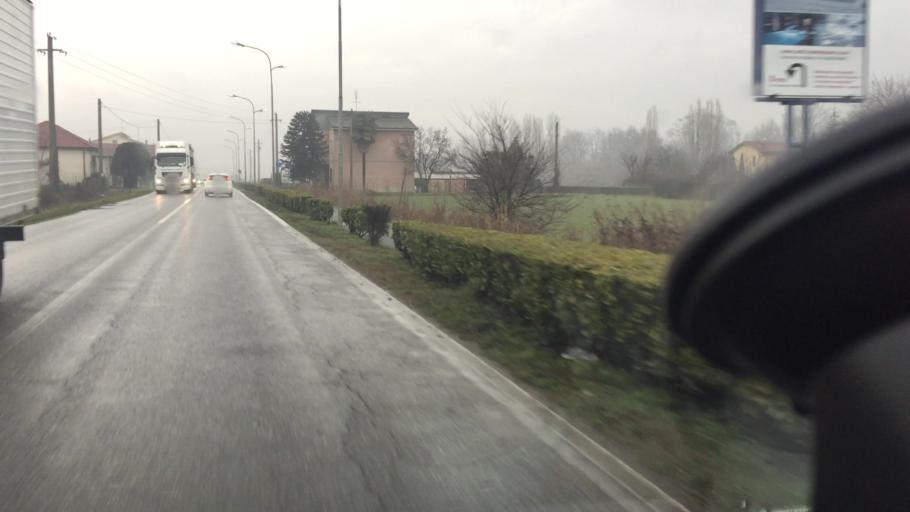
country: IT
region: Lombardy
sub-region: Citta metropolitana di Milano
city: Vaprio d'Adda
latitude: 45.5867
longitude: 9.5218
